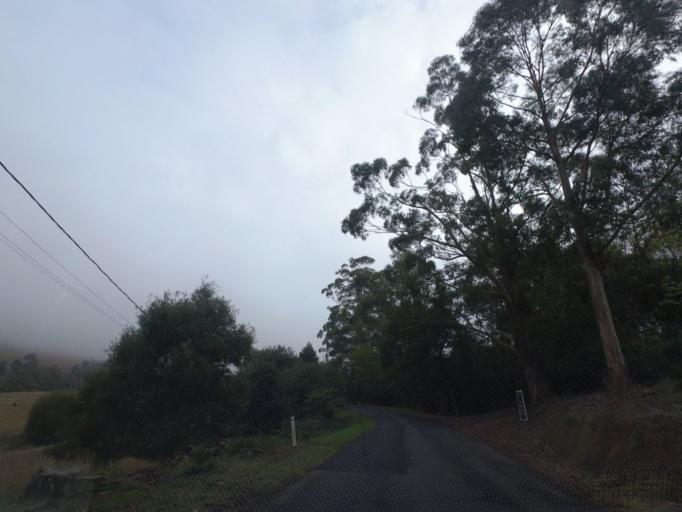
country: AU
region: Victoria
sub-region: Yarra Ranges
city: Yarra Junction
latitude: -37.7330
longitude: 145.5932
